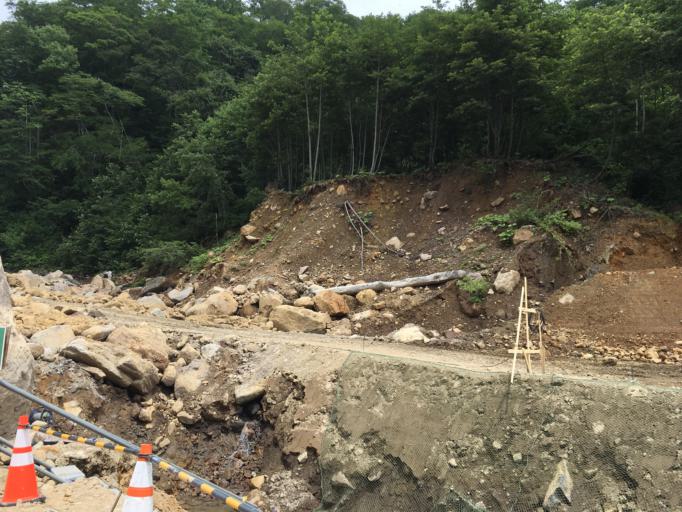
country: JP
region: Iwate
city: Ichinoseki
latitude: 38.9622
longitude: 140.8448
